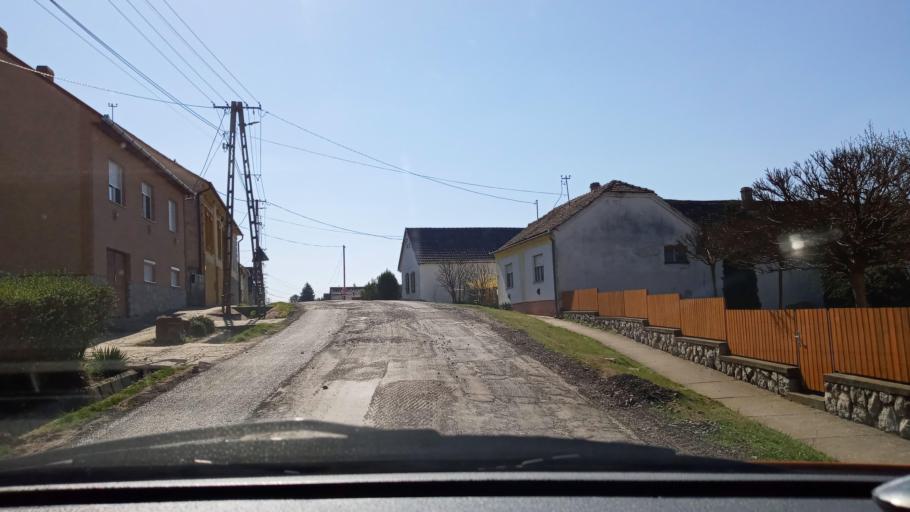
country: HU
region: Baranya
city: Boly
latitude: 46.0103
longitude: 18.4142
